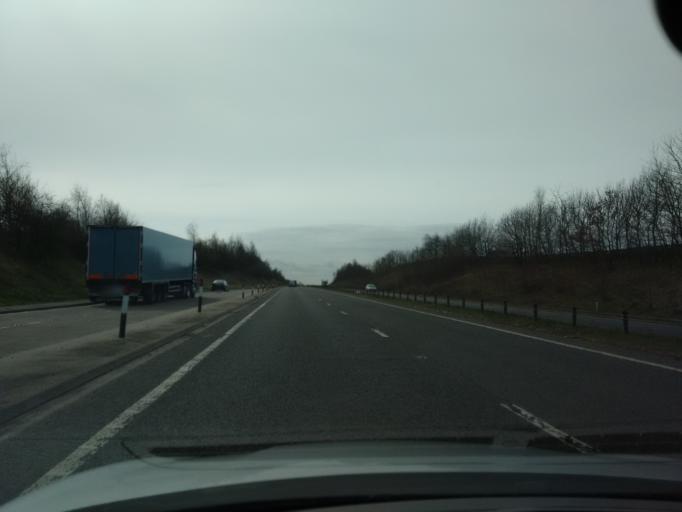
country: GB
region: England
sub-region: Warwickshire
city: Bidford-on-avon
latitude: 52.1858
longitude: -1.8772
